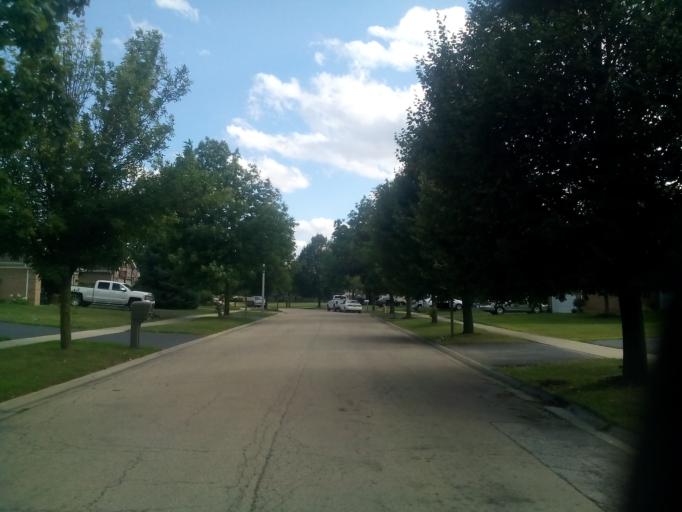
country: US
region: Illinois
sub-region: Will County
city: Romeoville
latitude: 41.6975
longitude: -88.1491
